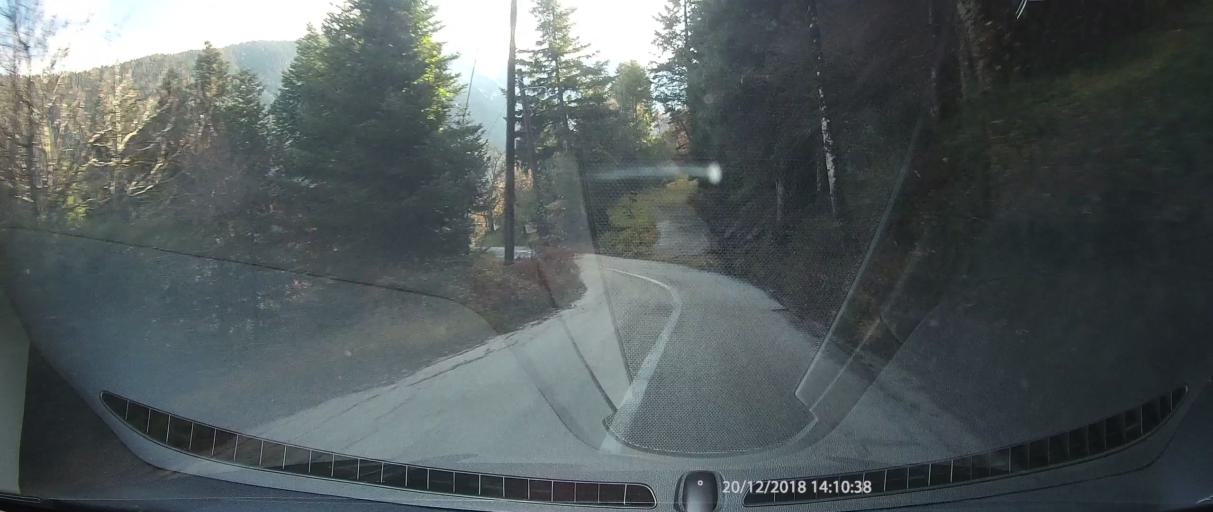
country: GR
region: West Greece
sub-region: Nomos Aitolias kai Akarnanias
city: Thermo
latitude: 38.7442
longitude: 21.6506
